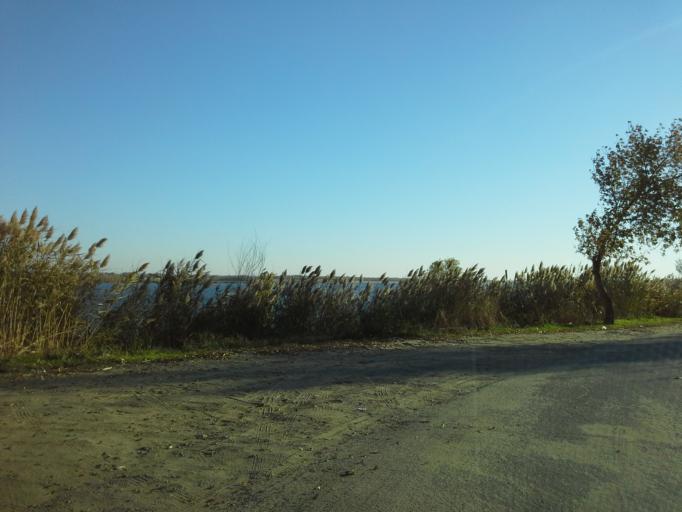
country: RU
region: Volgograd
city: Vodstroy
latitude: 48.8177
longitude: 44.6409
